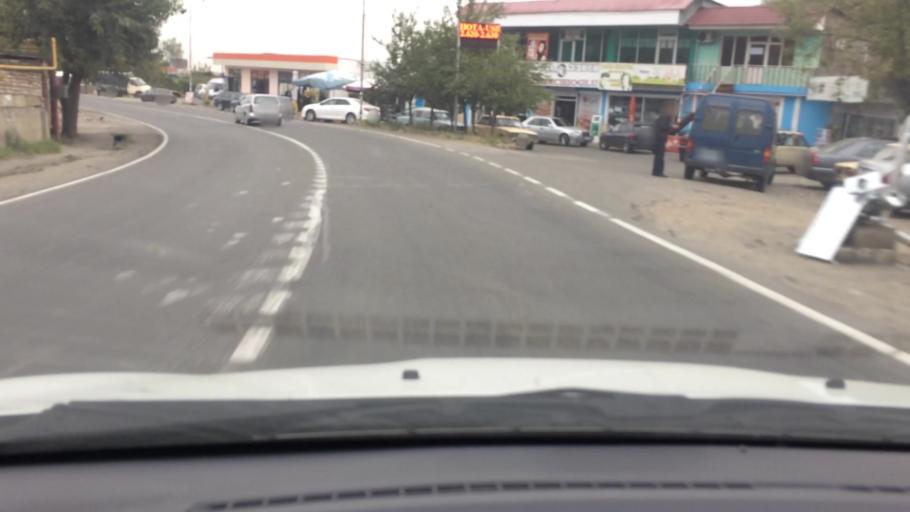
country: GE
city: Naghvarevi
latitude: 41.3656
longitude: 44.8399
